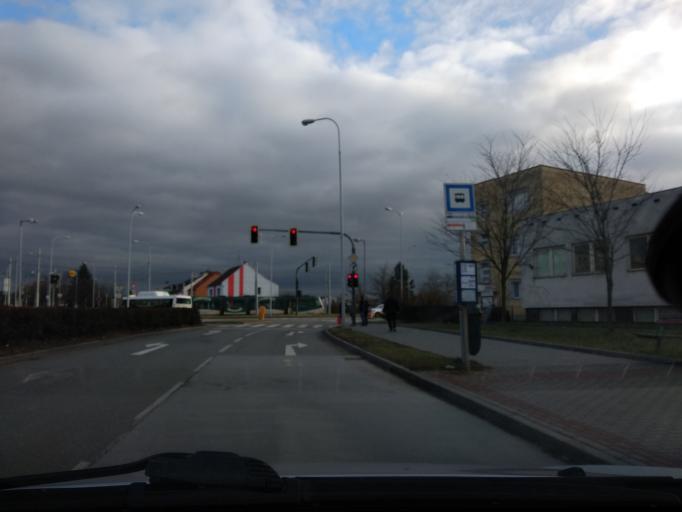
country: CZ
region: South Moravian
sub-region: Mesto Brno
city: Brno
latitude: 49.2232
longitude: 16.6224
